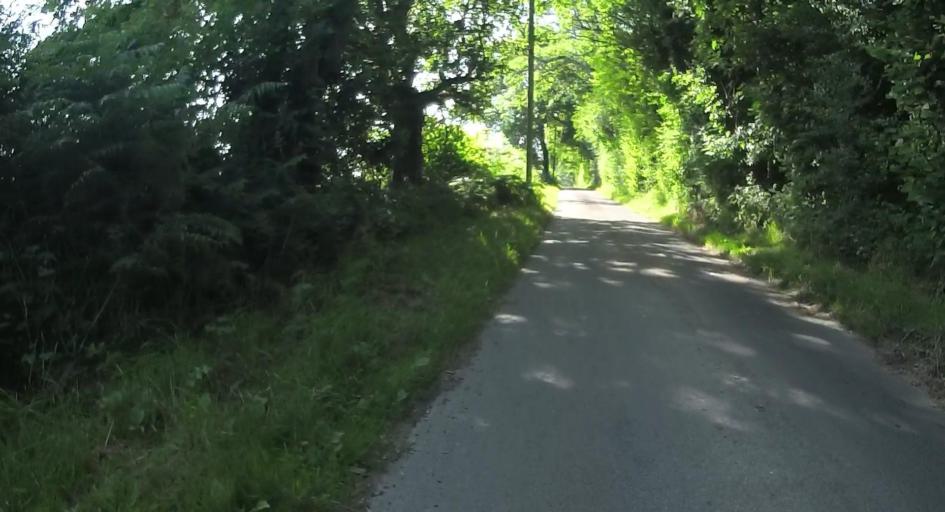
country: GB
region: England
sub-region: Hampshire
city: Long Sutton
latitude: 51.1903
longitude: -0.9531
